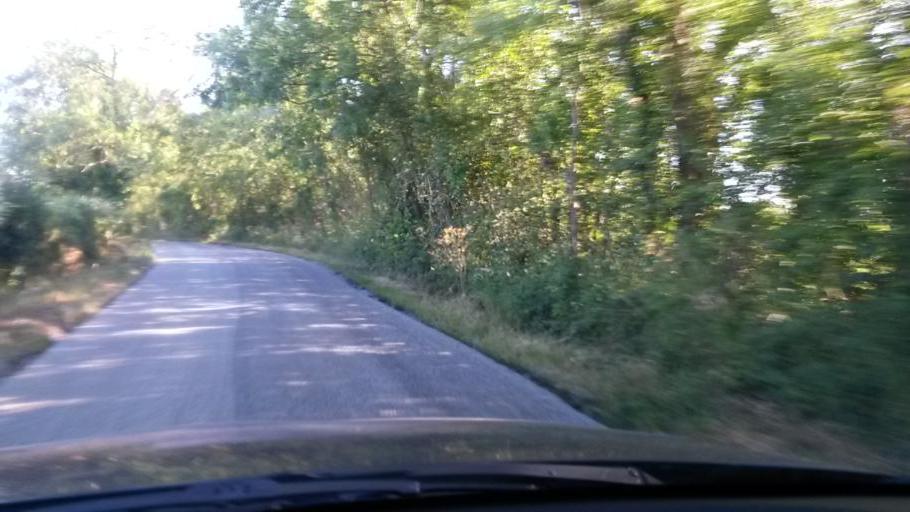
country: IE
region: Leinster
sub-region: An Mhi
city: Ashbourne
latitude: 53.4966
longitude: -6.3062
